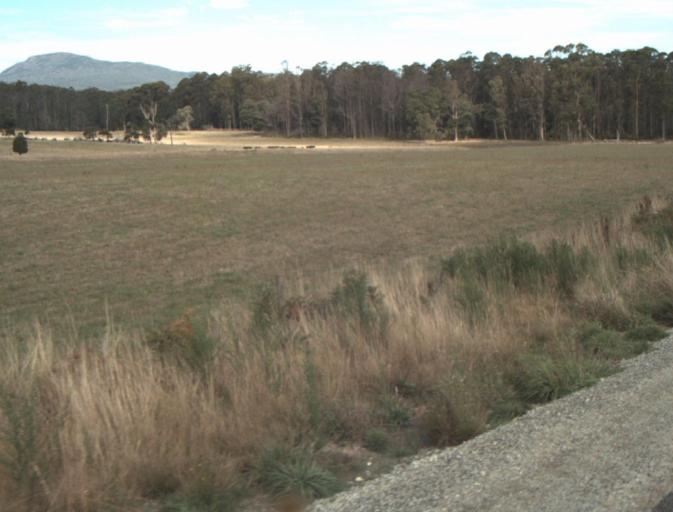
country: AU
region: Tasmania
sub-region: Launceston
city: Mayfield
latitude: -41.2016
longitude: 147.1894
